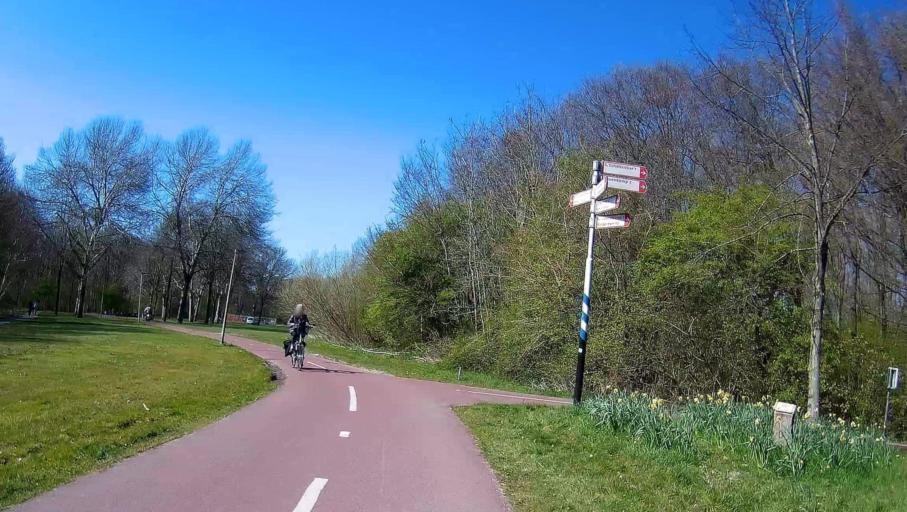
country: NL
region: South Holland
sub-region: Gemeente Capelle aan den IJssel
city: Capelle aan den IJssel
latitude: 51.9442
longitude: 4.5853
